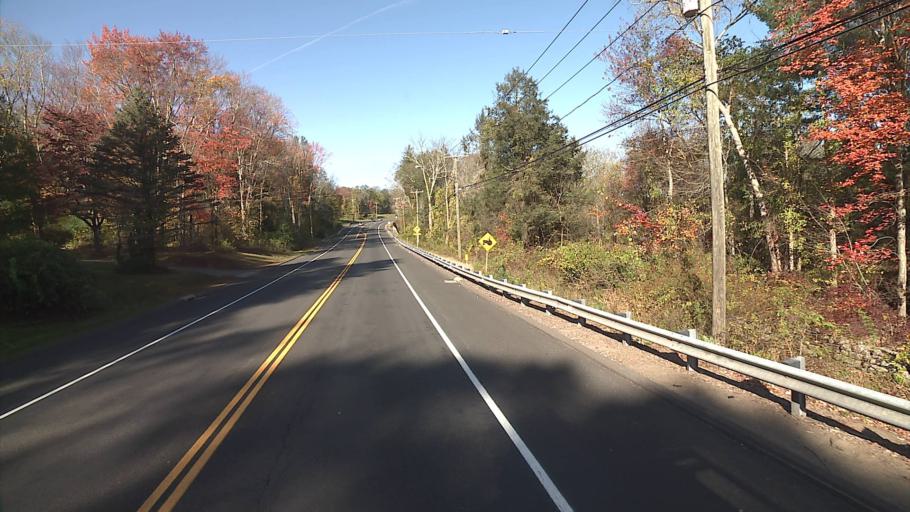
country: US
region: Connecticut
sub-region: Tolland County
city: Coventry Lake
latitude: 41.7477
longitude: -72.3916
